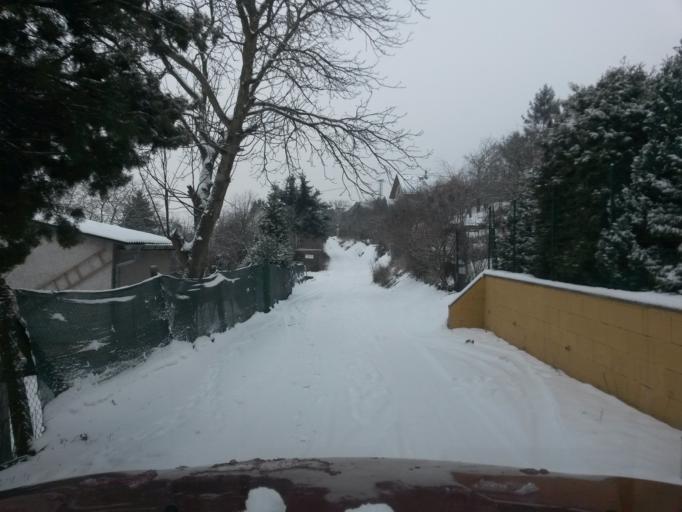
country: SK
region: Kosicky
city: Kosice
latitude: 48.7229
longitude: 21.3272
